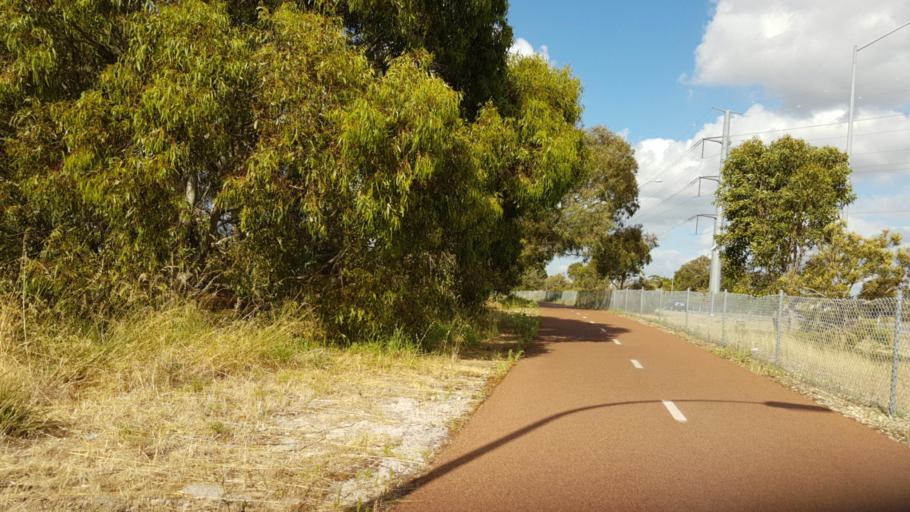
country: AU
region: Western Australia
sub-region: Gosnells
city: Langford
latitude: -32.0517
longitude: 115.9358
